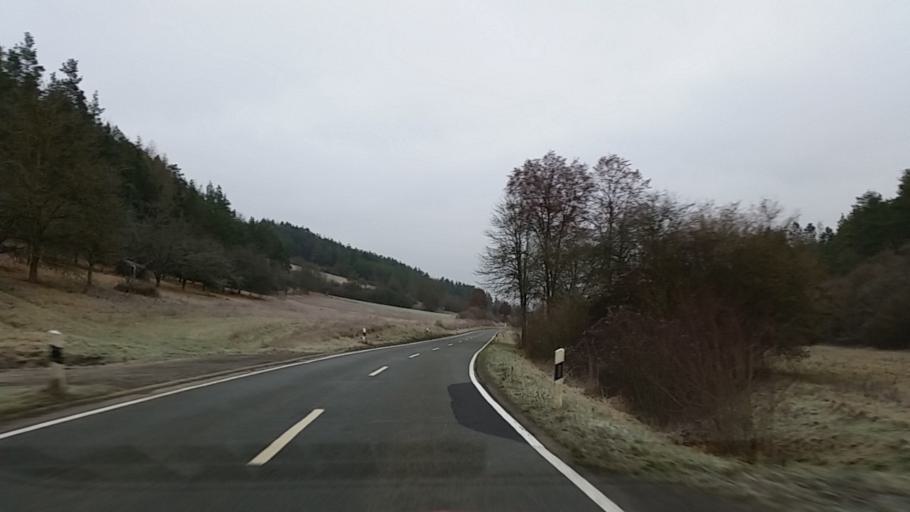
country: DE
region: Bavaria
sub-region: Regierungsbezirk Unterfranken
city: Fuchsstadt
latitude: 50.0963
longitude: 9.9256
